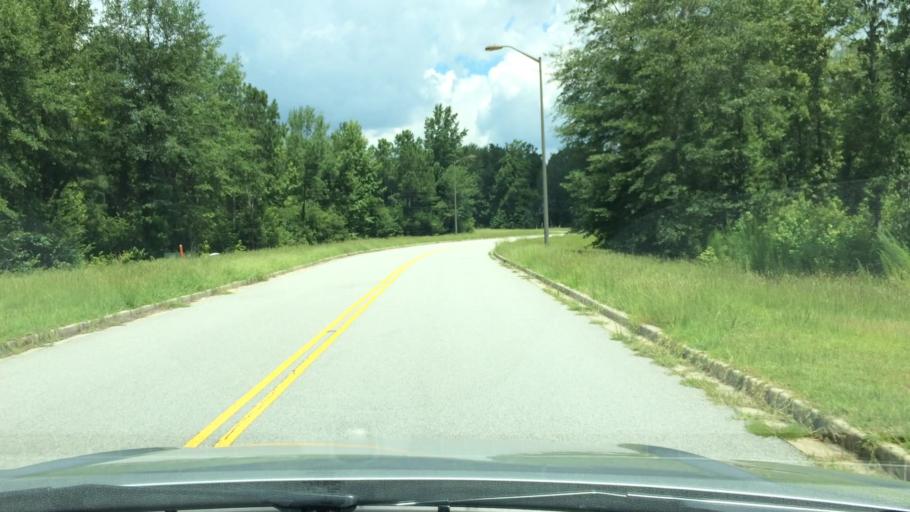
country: US
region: South Carolina
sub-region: Calhoun County
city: Oak Grove
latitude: 33.8004
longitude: -81.0051
